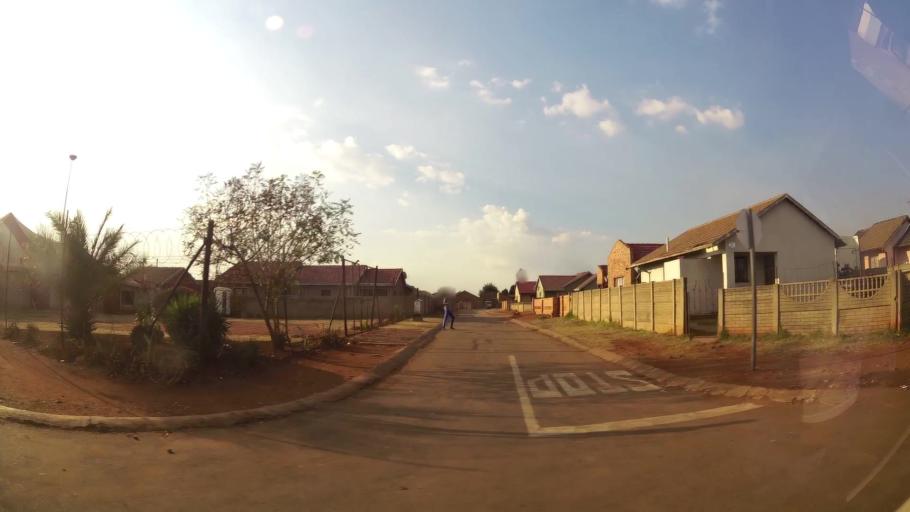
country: ZA
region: Gauteng
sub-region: Ekurhuleni Metropolitan Municipality
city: Germiston
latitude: -26.3481
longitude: 28.2125
